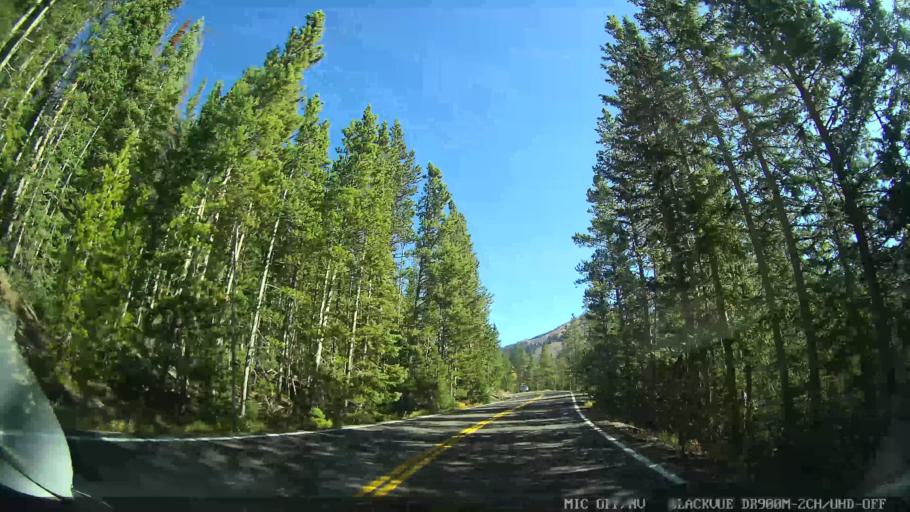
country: US
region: Colorado
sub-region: Larimer County
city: Estes Park
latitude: 40.4037
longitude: -105.8251
